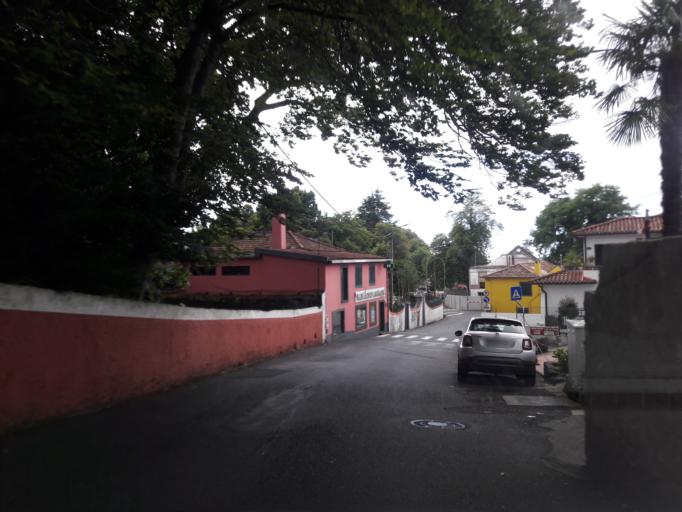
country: PT
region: Madeira
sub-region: Santa Cruz
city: Camacha
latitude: 32.6807
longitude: -16.8459
